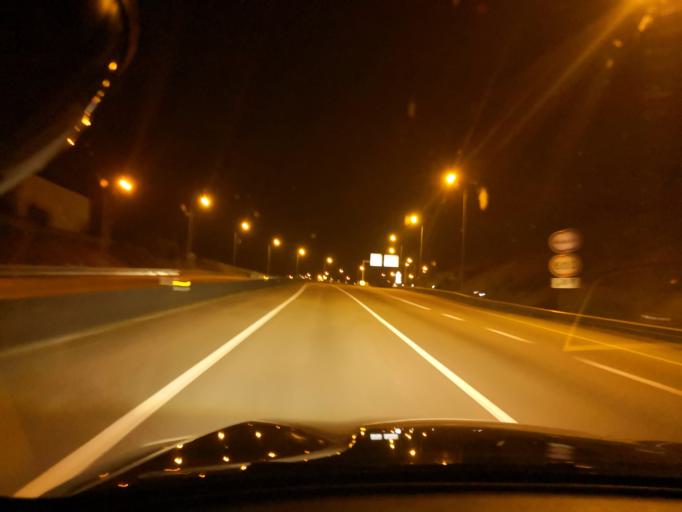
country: PT
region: Aveiro
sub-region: Albergaria-A-Velha
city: Albergaria-a-Velha
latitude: 40.6762
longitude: -8.4685
